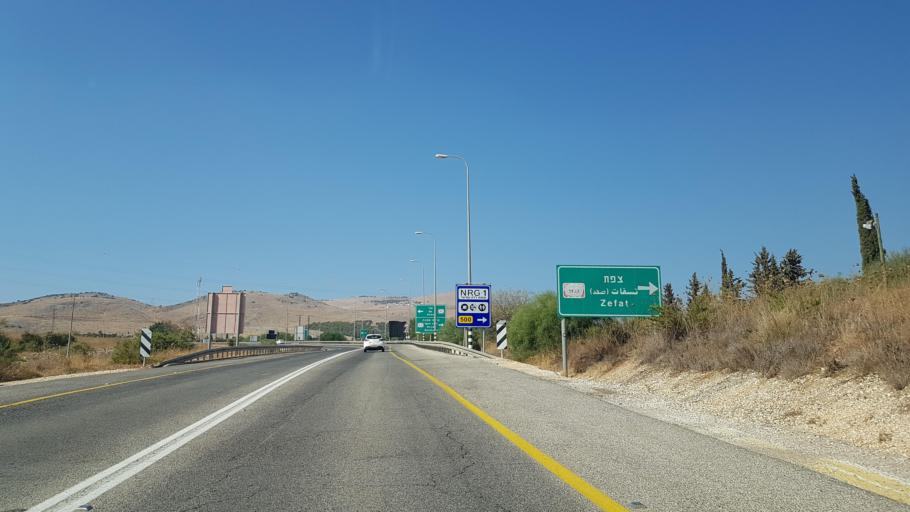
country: IL
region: Northern District
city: Rosh Pinna
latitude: 32.9110
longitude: 35.5460
